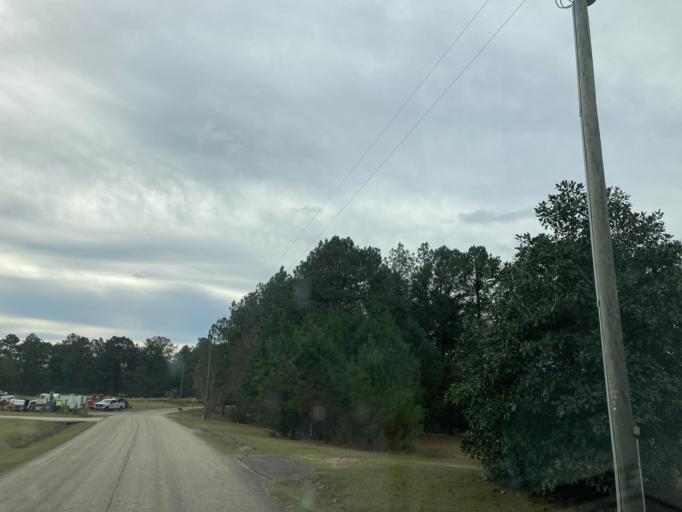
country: US
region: Mississippi
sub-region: Lamar County
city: Purvis
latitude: 31.1446
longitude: -89.4611
